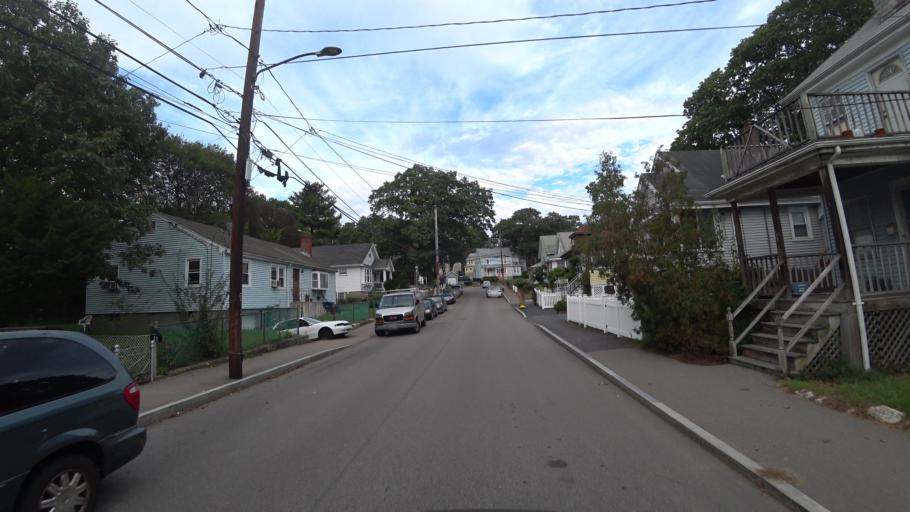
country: US
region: Massachusetts
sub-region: Suffolk County
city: Jamaica Plain
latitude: 42.2692
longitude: -71.1098
